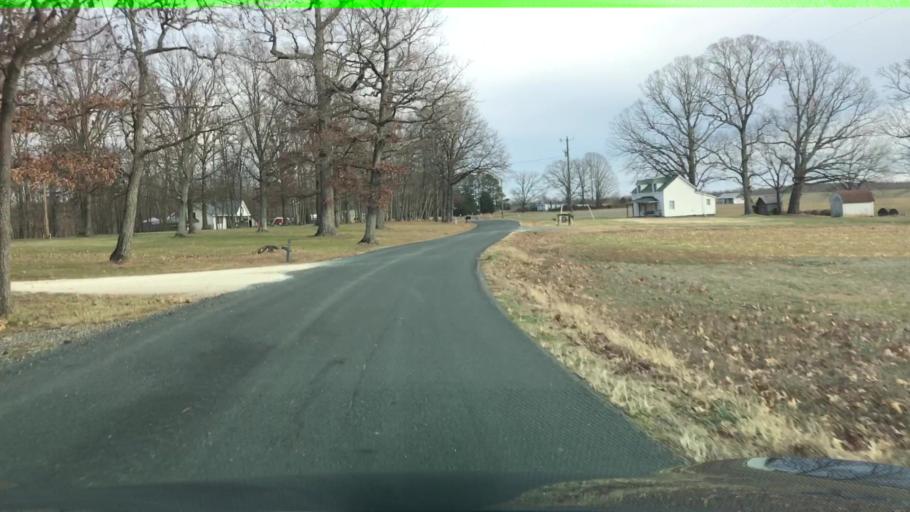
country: US
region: Virginia
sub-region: Campbell County
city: Concord
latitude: 37.2487
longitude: -78.8909
